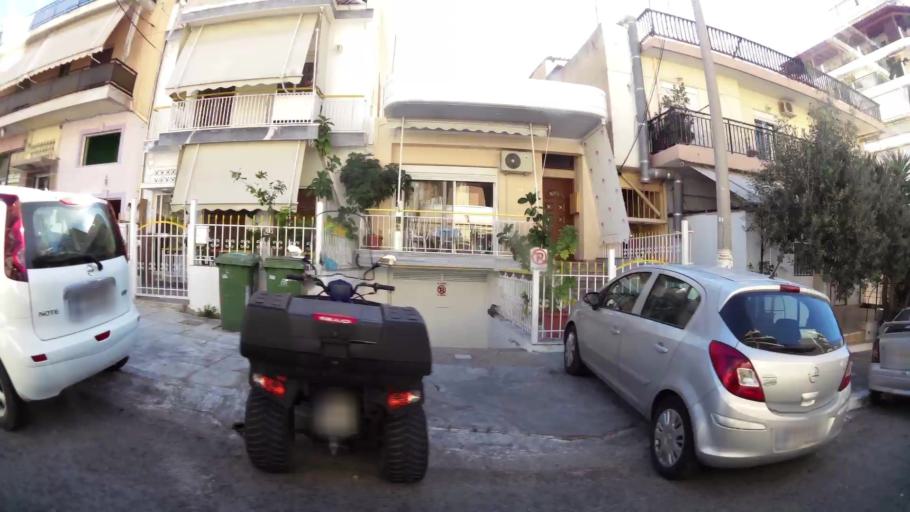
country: GR
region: Attica
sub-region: Nomos Piraios
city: Perama
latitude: 37.9670
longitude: 23.5714
